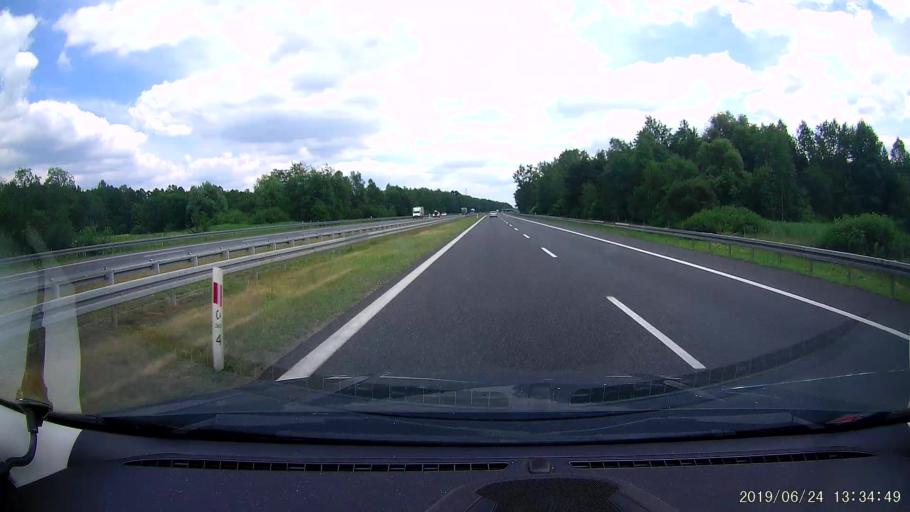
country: PL
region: Lesser Poland Voivodeship
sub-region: Powiat oswiecimski
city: Chelmek
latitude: 50.1496
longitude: 19.2731
